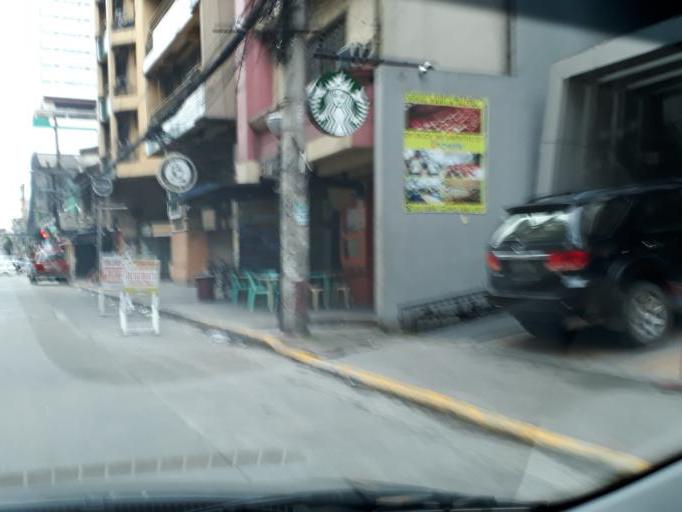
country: PH
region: Metro Manila
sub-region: City of Manila
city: Manila
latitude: 14.6074
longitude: 120.9888
